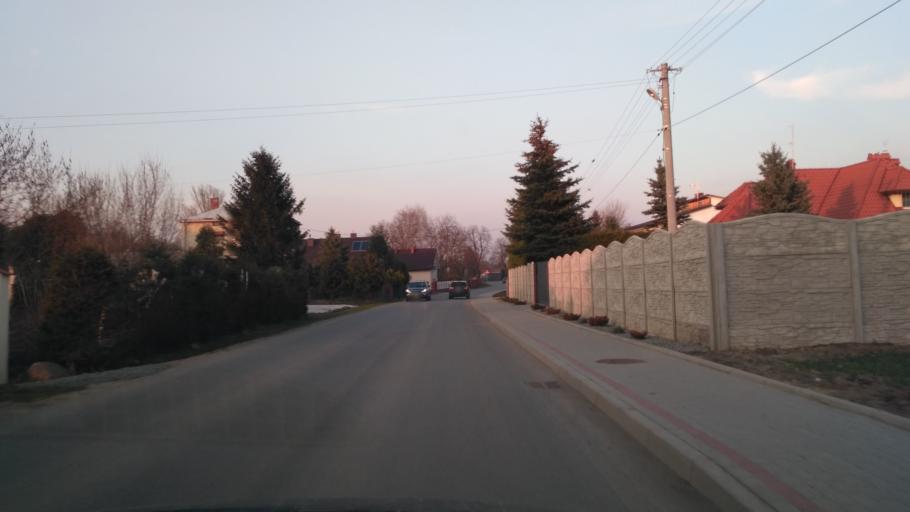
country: PL
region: Subcarpathian Voivodeship
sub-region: Powiat przeworski
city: Zurawiczki
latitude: 50.0059
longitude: 22.4815
